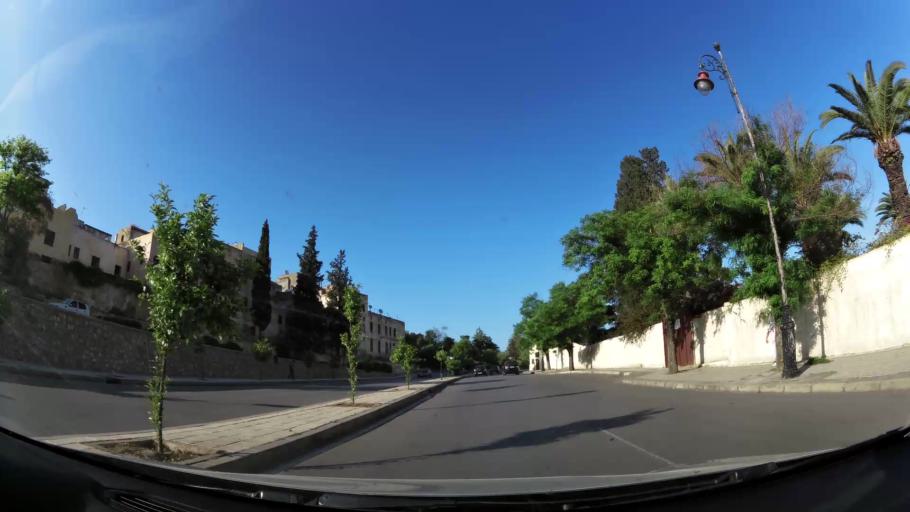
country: MA
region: Fes-Boulemane
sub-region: Fes
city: Fes
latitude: 34.0517
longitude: -4.9897
